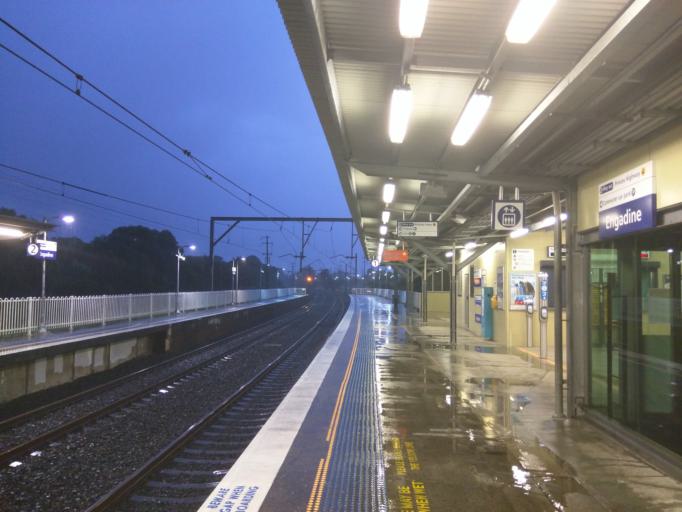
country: AU
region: New South Wales
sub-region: Sutherland Shire
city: Engadine
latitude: -34.0678
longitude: 151.0147
